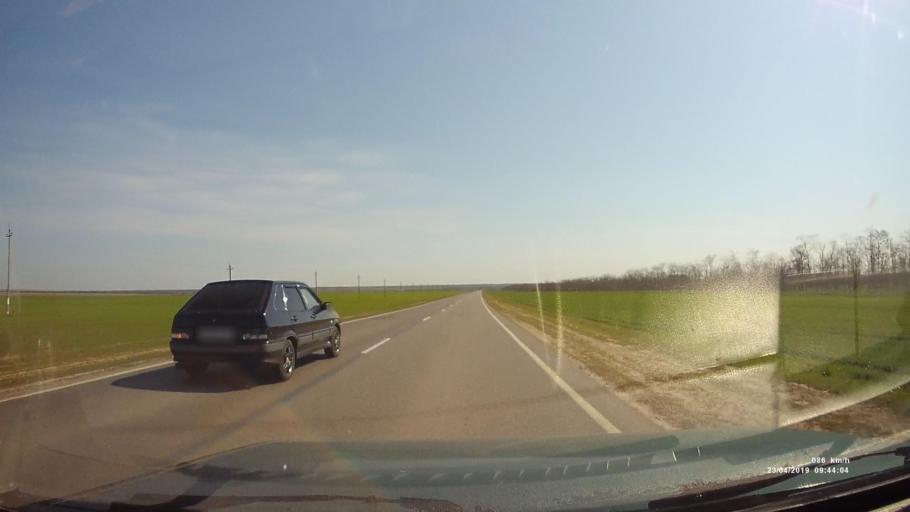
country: RU
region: Rostov
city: Orlovskiy
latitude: 46.8788
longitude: 42.0073
